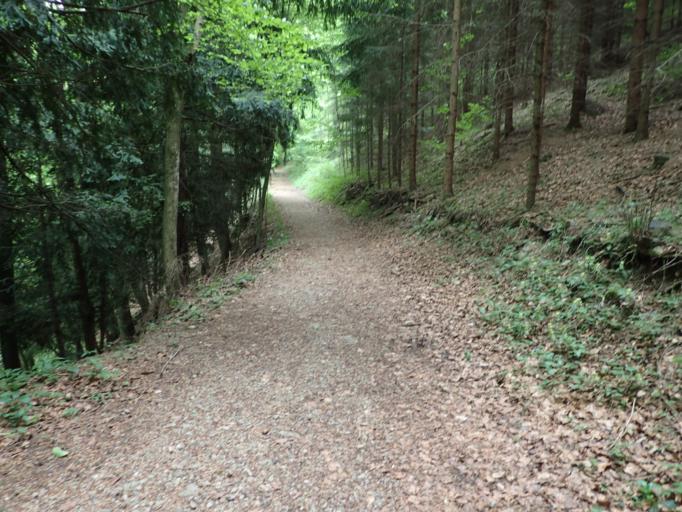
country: AT
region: Salzburg
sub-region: Politischer Bezirk Salzburg-Umgebung
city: Elsbethen
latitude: 47.7473
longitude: 13.0980
